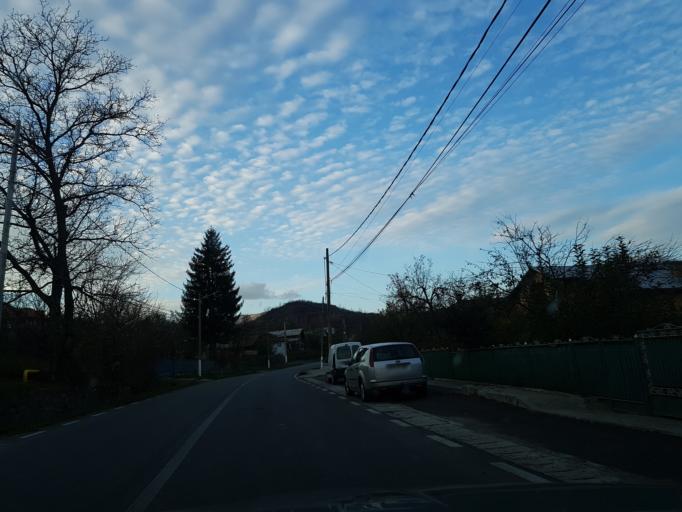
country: RO
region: Prahova
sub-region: Oras Breaza
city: Gura Beliei
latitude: 45.2191
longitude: 25.6396
